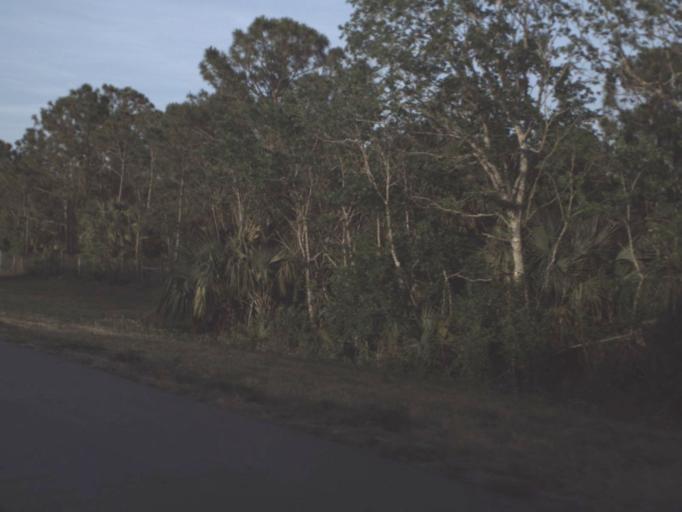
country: US
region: Florida
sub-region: Brevard County
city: Mims
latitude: 28.7358
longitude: -80.8851
